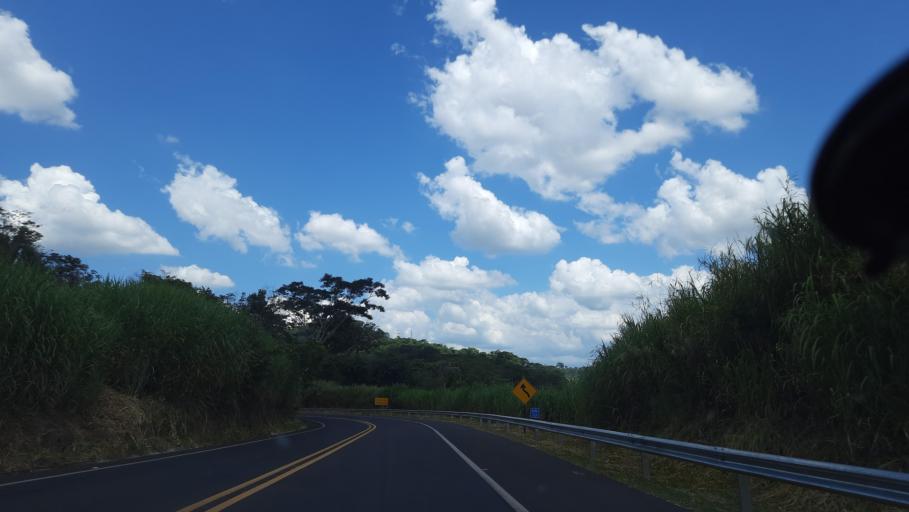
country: BR
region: Sao Paulo
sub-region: Sao Jose Do Rio Pardo
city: Sao Jose do Rio Pardo
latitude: -21.6036
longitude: -46.9579
